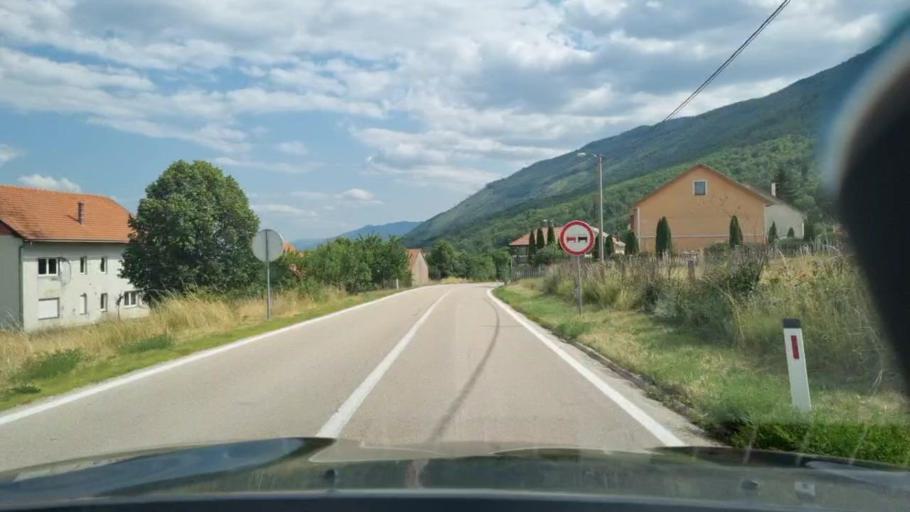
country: BA
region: Federation of Bosnia and Herzegovina
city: Bosansko Grahovo
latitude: 44.0796
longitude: 16.5708
